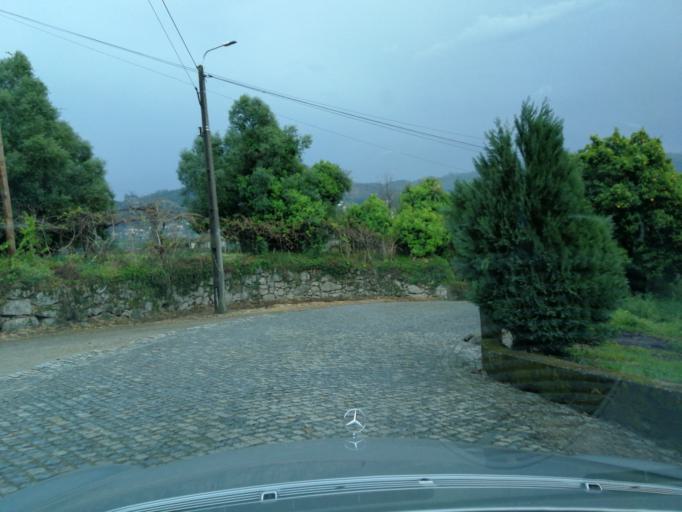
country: PT
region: Braga
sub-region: Braga
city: Oliveira
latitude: 41.4540
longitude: -8.4605
